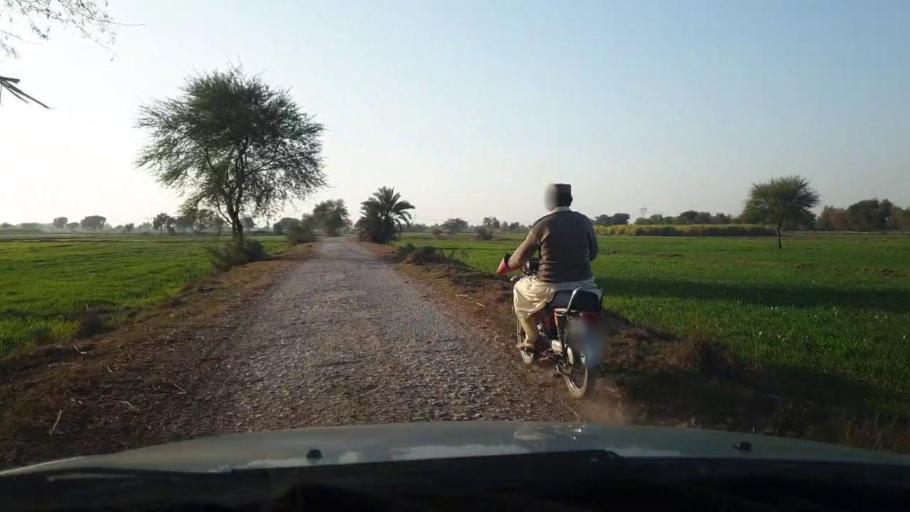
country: PK
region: Sindh
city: Mirpur Mathelo
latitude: 28.0003
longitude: 69.5085
